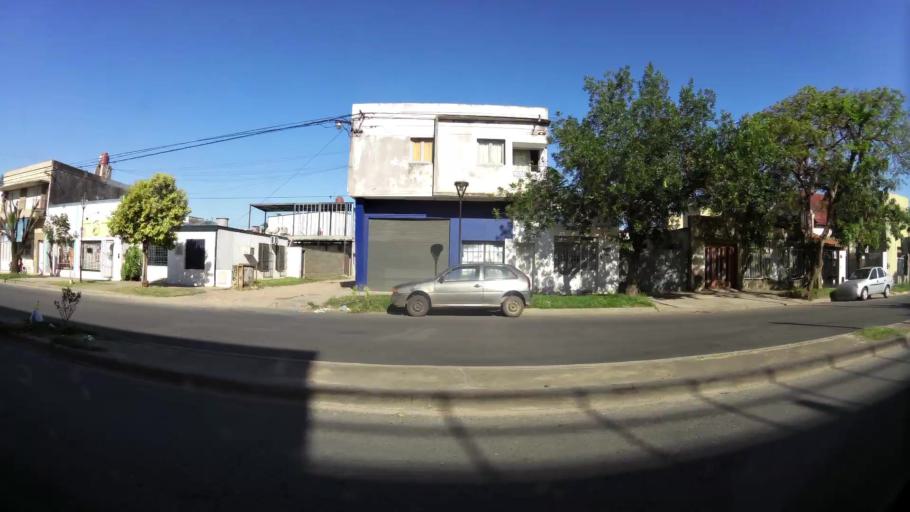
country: AR
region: Santa Fe
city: Santa Fe de la Vera Cruz
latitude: -31.6079
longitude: -60.7041
